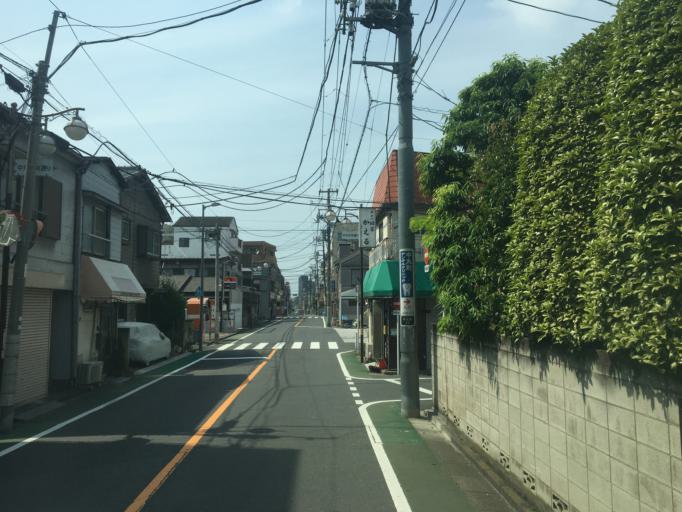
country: JP
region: Tokyo
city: Tokyo
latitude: 35.7410
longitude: 139.7022
